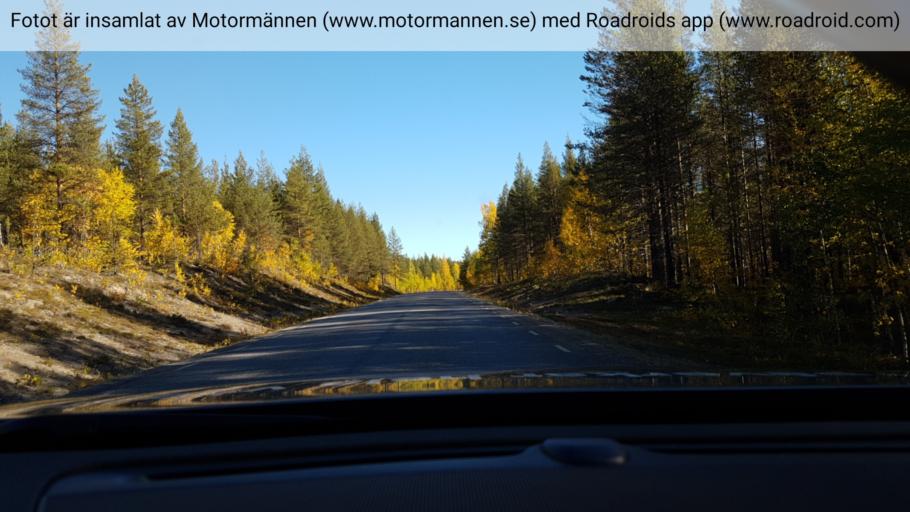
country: SE
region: Norrbotten
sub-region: Gallivare Kommun
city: Gaellivare
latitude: 66.4514
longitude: 20.6999
